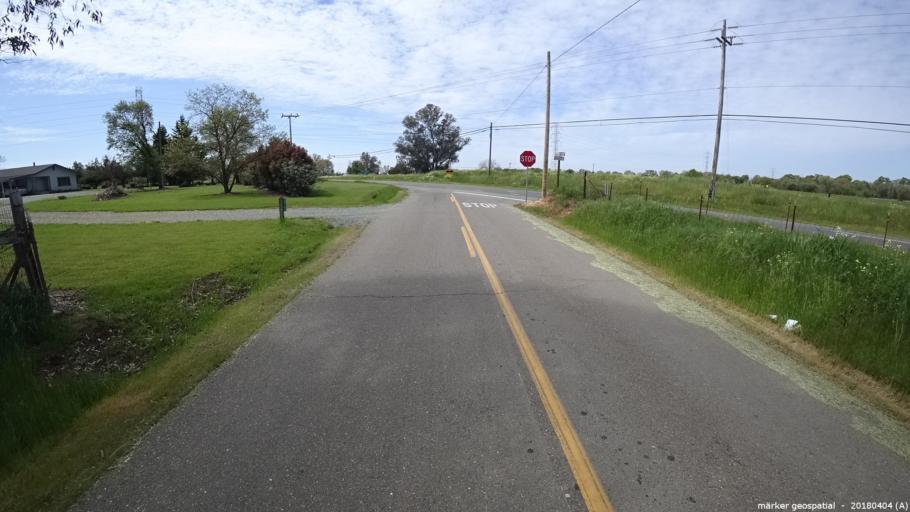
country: US
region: California
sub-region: Sacramento County
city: Herald
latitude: 38.3067
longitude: -121.2242
